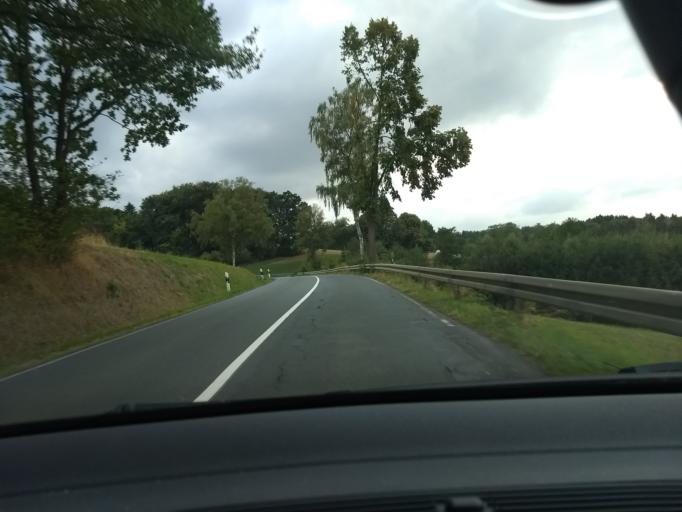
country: DE
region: North Rhine-Westphalia
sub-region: Regierungsbezirk Arnsberg
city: Arnsberg
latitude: 51.3396
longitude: 8.1138
